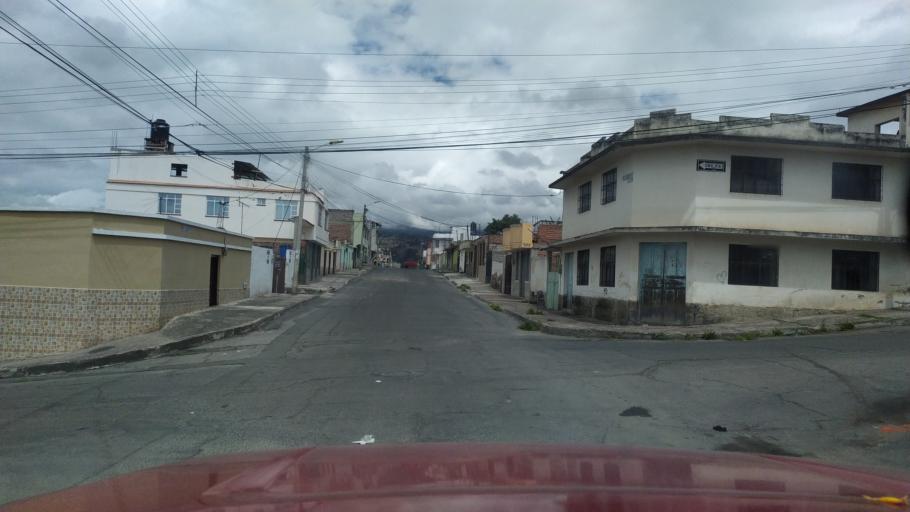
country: EC
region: Chimborazo
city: Riobamba
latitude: -1.6666
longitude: -78.6408
